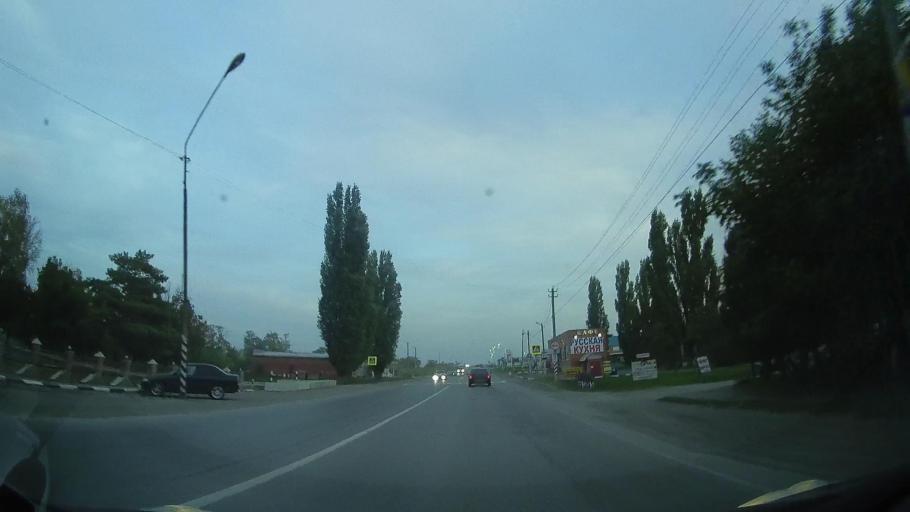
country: RU
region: Rostov
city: Kagal'nitskaya
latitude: 46.8781
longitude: 40.1555
